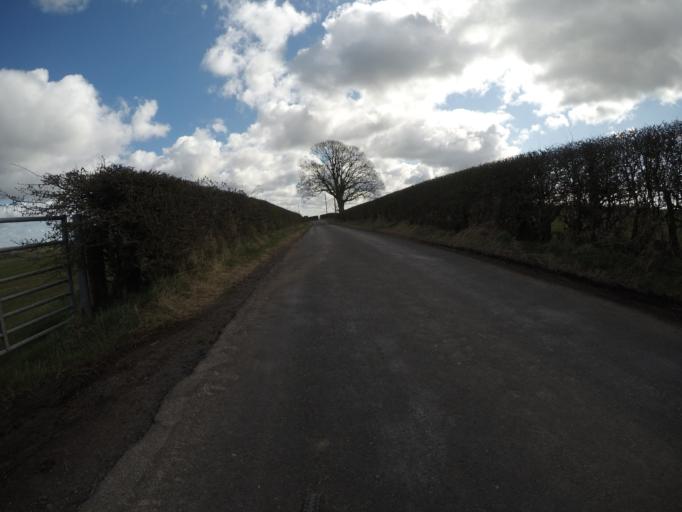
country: GB
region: Scotland
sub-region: South Ayrshire
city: Dundonald
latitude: 55.5892
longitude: -4.5893
